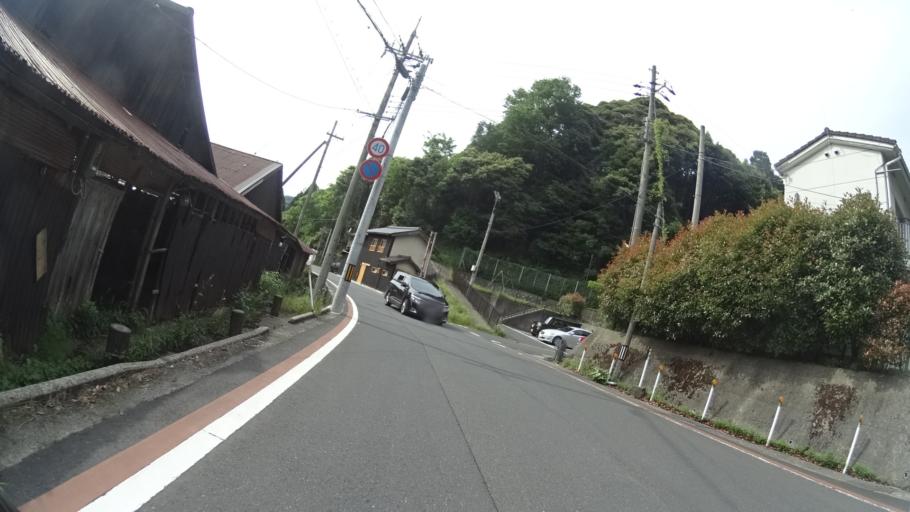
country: JP
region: Kyoto
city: Miyazu
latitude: 35.6710
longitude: 135.2769
